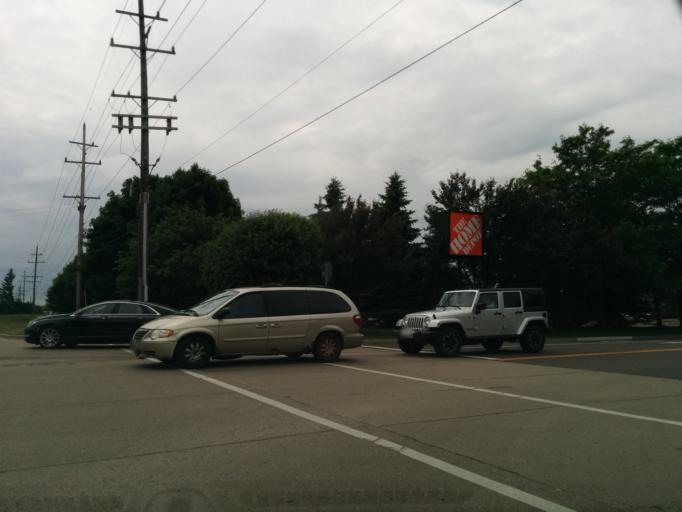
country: US
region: Michigan
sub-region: Oakland County
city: Wolverine Lake
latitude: 42.5329
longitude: -83.4380
